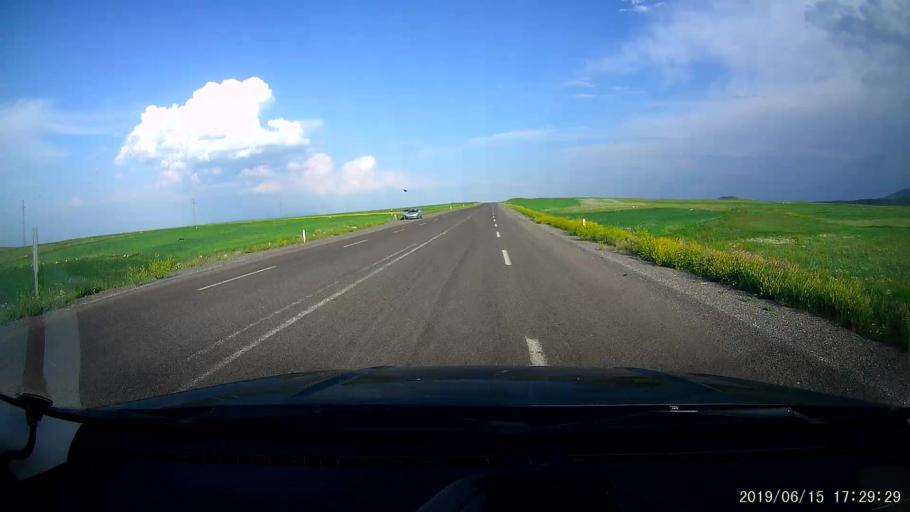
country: TR
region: Kars
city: Basgedikler
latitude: 40.5894
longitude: 43.4528
